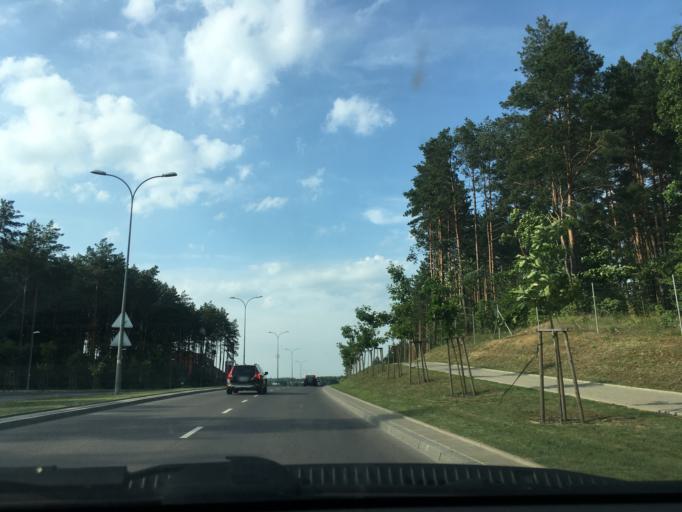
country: PL
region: Podlasie
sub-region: Bialystok
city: Bialystok
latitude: 53.1310
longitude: 23.2223
